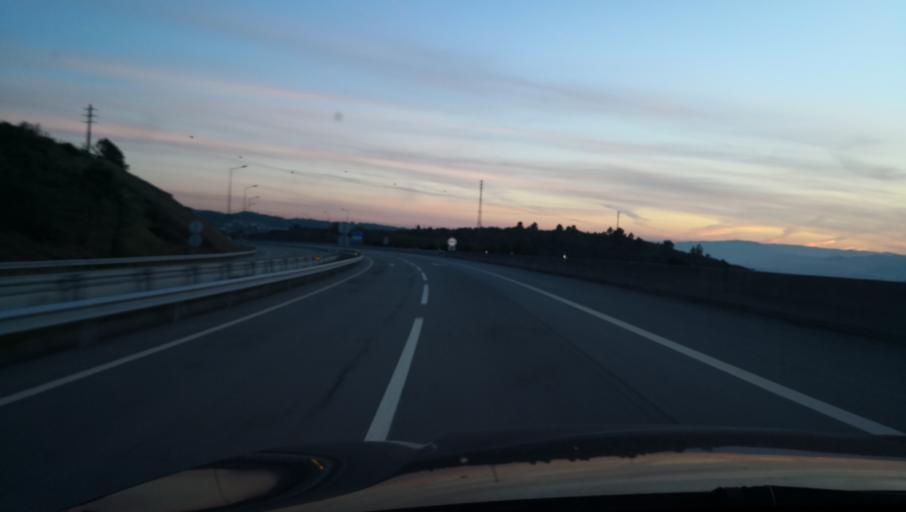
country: PT
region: Vila Real
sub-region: Vila Real
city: Vila Real
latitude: 41.3424
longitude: -7.7059
